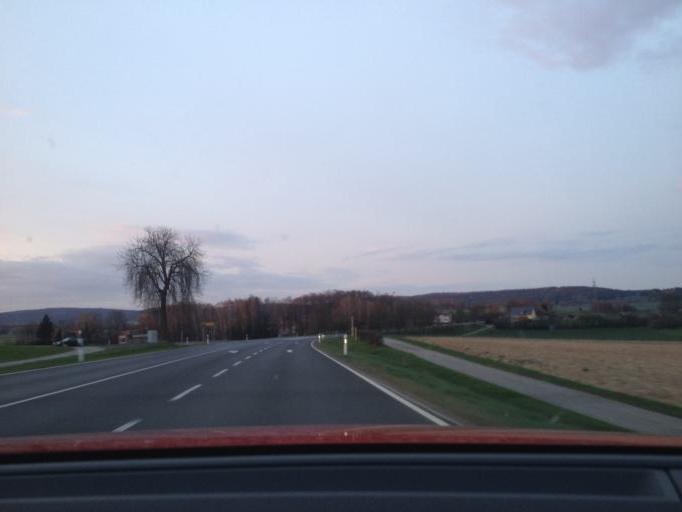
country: DE
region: Bavaria
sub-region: Upper Palatinate
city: Kemnath
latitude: 49.8823
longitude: 11.8875
